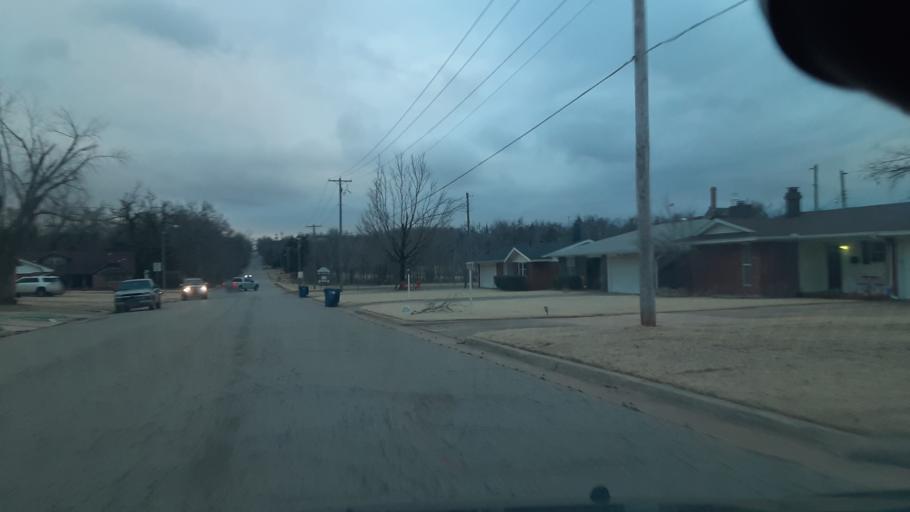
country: US
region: Oklahoma
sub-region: Logan County
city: Guthrie
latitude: 35.8890
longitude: -97.4163
